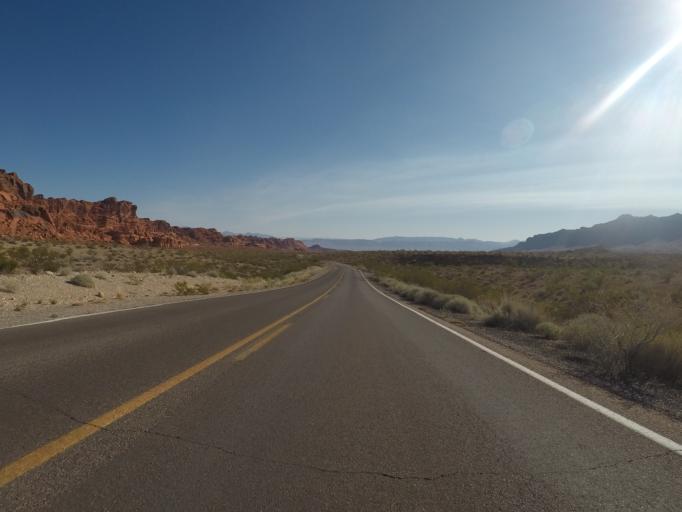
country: US
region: Nevada
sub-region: Clark County
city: Moapa Valley
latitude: 36.4252
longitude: -114.5326
